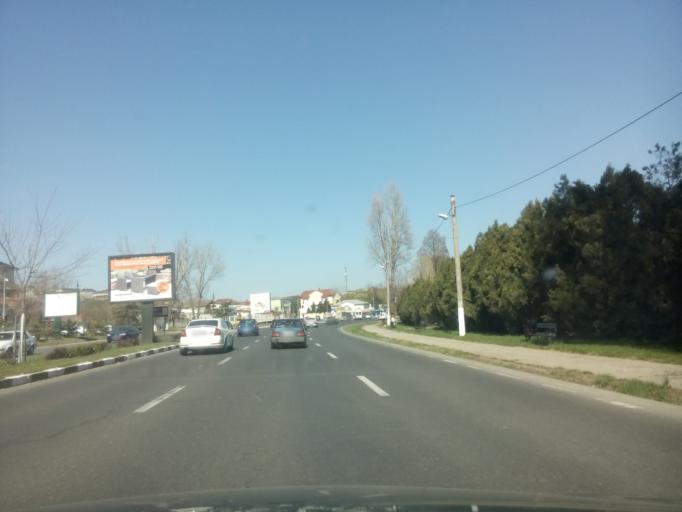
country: RO
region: Ilfov
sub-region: Comuna Pantelimon
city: Pantelimon
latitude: 44.4470
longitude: 26.2032
